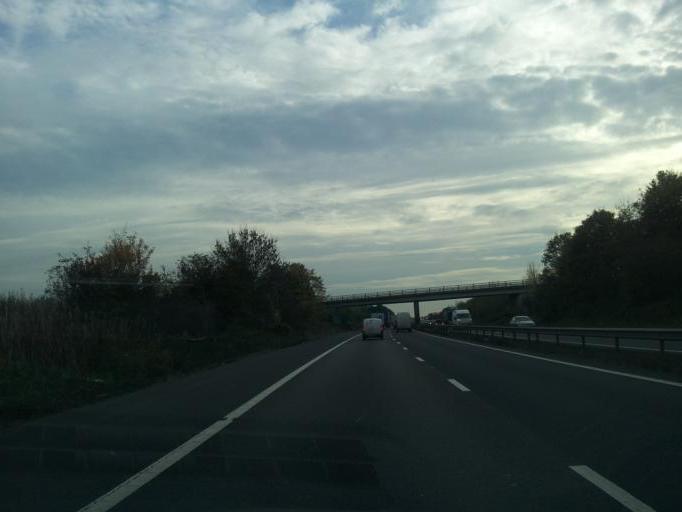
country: GB
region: England
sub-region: Cambridgeshire
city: Duxford
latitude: 52.1173
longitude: 0.1272
